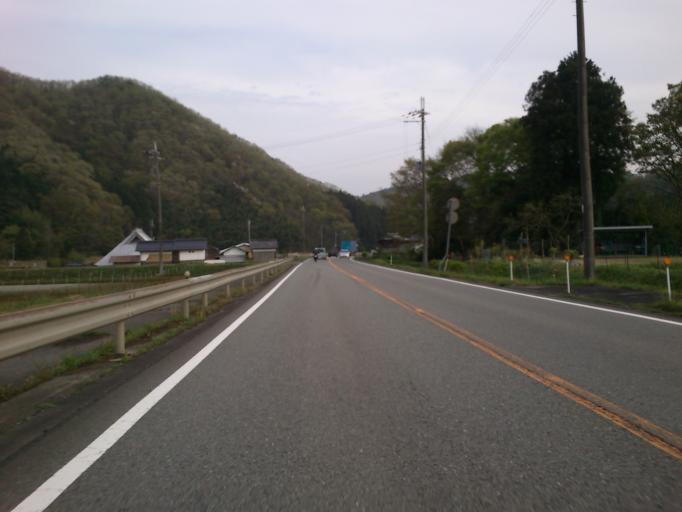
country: JP
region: Hyogo
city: Sasayama
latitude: 35.1261
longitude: 135.3357
